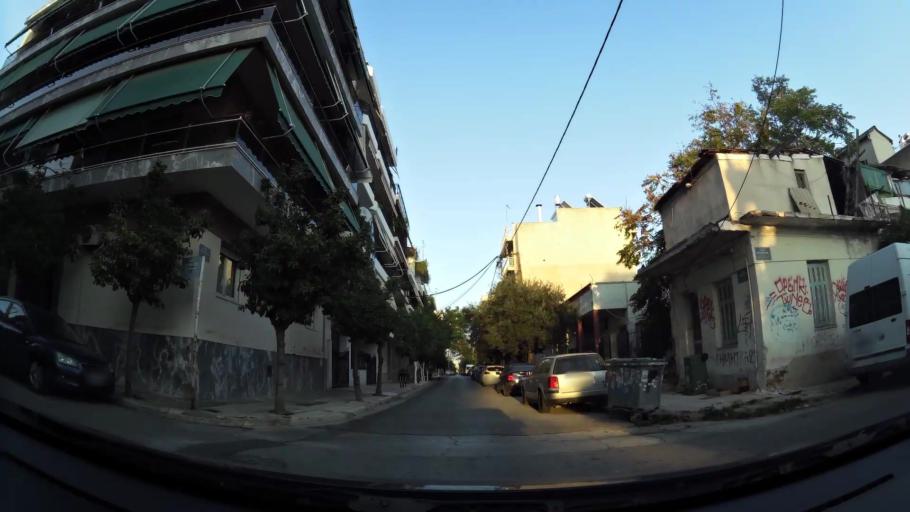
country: GR
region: Attica
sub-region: Nomos Piraios
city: Nikaia
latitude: 37.9687
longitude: 23.6423
